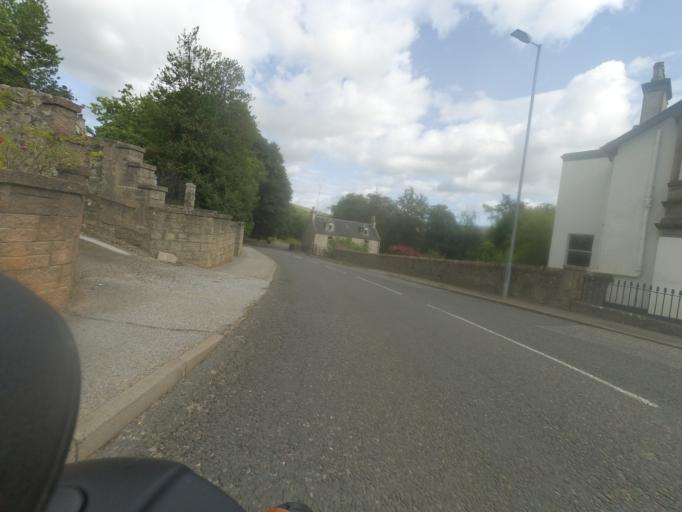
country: GB
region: Scotland
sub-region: Moray
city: Dufftown
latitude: 57.4441
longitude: -3.1226
